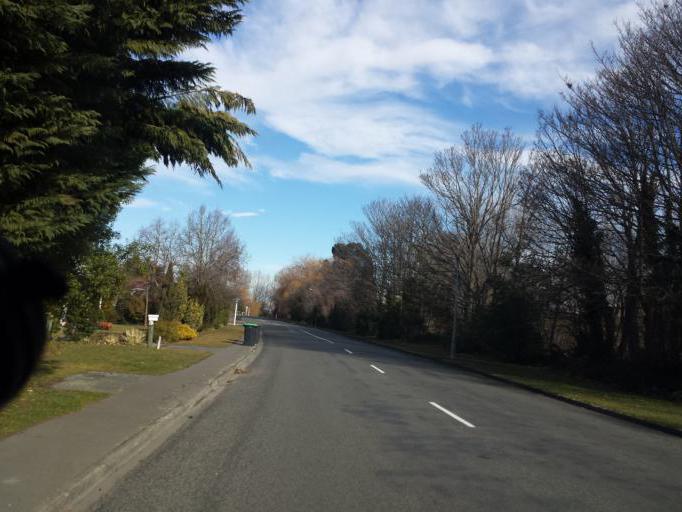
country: NZ
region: Canterbury
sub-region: Timaru District
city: Pleasant Point
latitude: -44.0864
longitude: 171.2457
